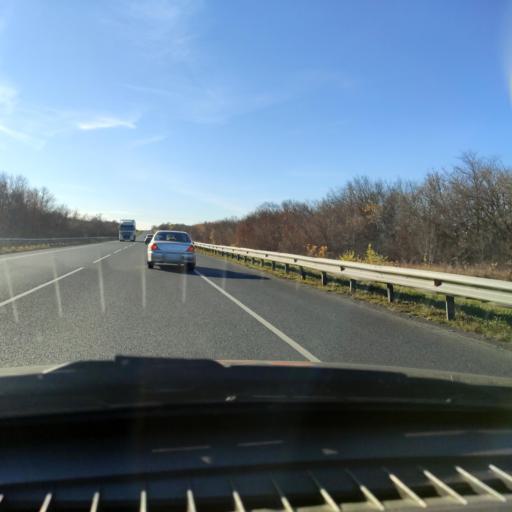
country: RU
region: Samara
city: Mezhdurechensk
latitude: 53.2558
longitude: 49.0542
